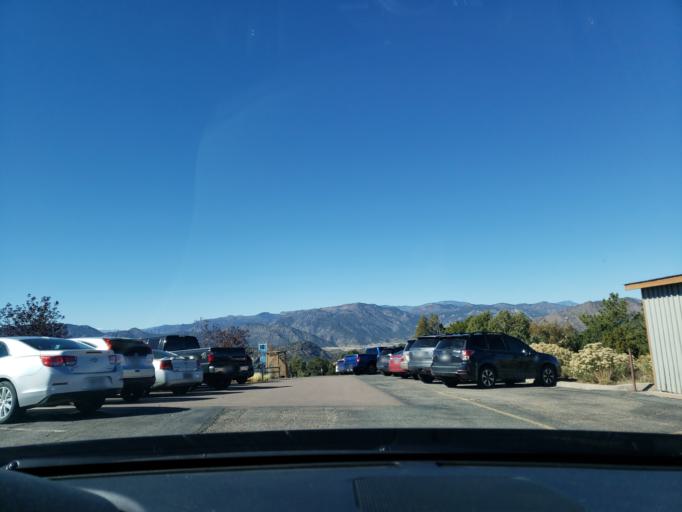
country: US
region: Colorado
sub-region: Fremont County
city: Canon City
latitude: 38.4635
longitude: -105.3202
